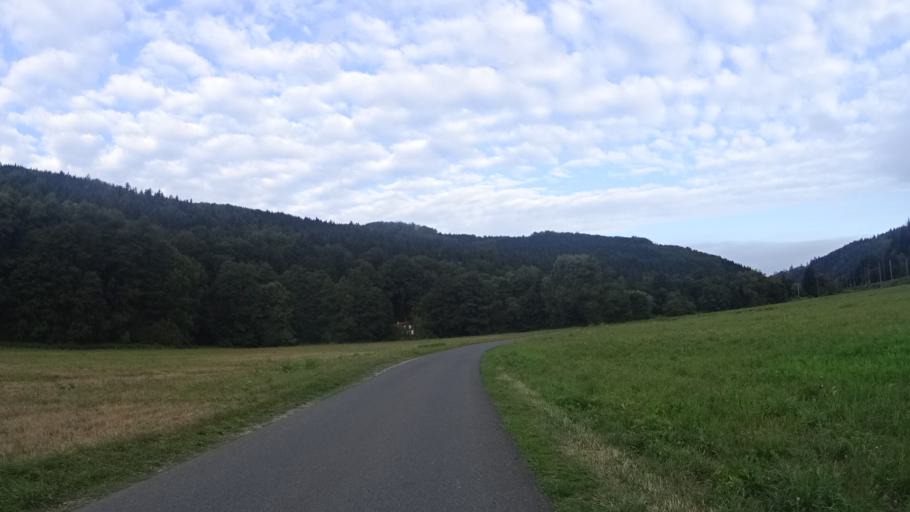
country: CZ
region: Olomoucky
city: Zabreh
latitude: 49.8660
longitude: 16.7948
